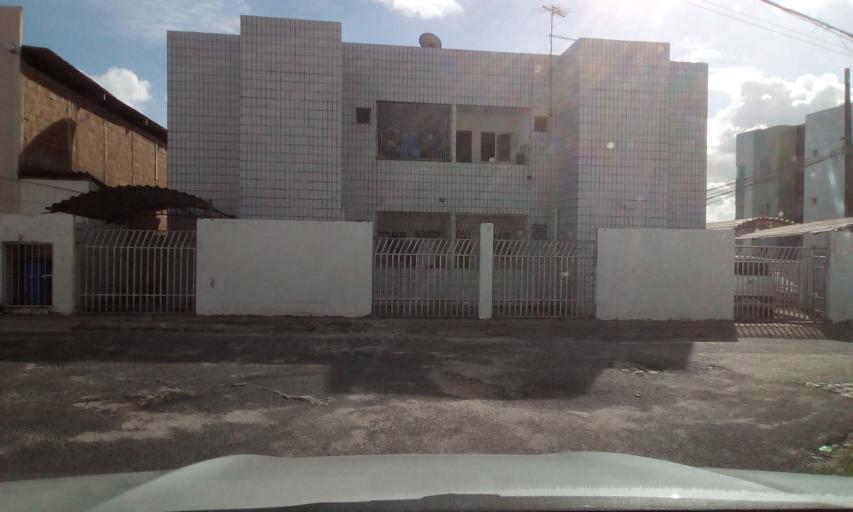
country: BR
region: Paraiba
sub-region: Joao Pessoa
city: Joao Pessoa
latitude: -7.1761
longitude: -34.8419
